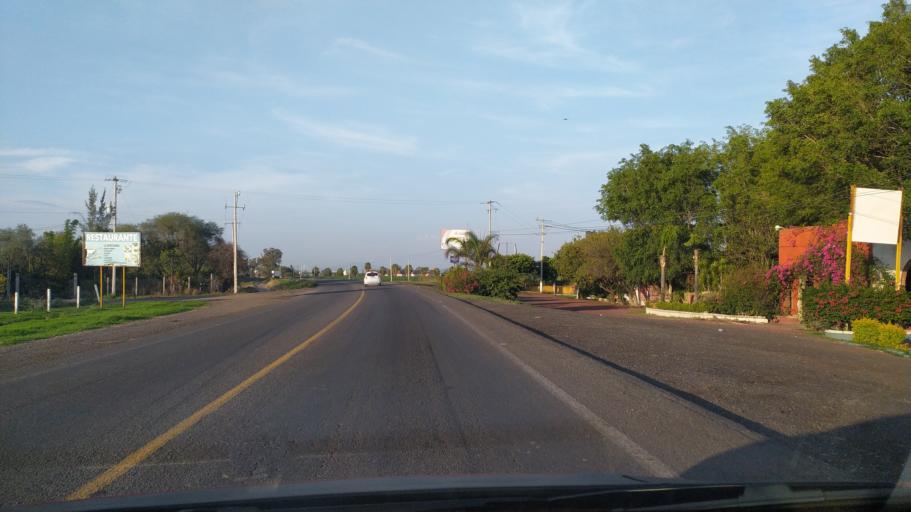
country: MX
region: Michoacan
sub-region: Brisenas
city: Paso de Hidalgo (Paso de Alamos)
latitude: 20.2680
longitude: -102.5310
